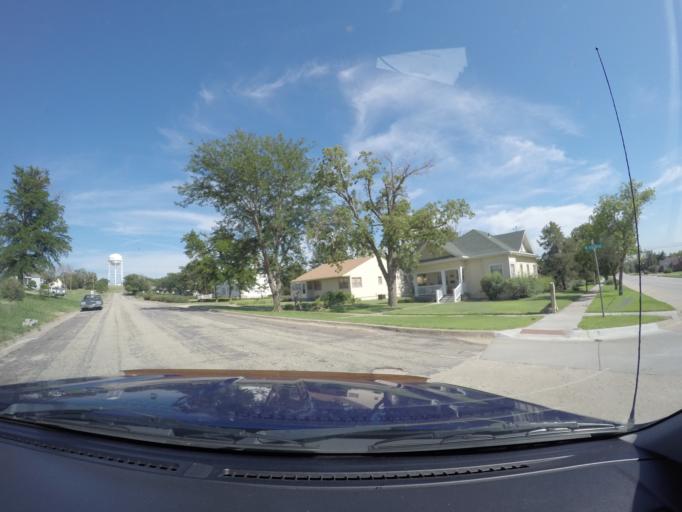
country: US
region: Kansas
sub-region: Rooks County
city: Stockton
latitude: 39.4412
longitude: -99.2750
